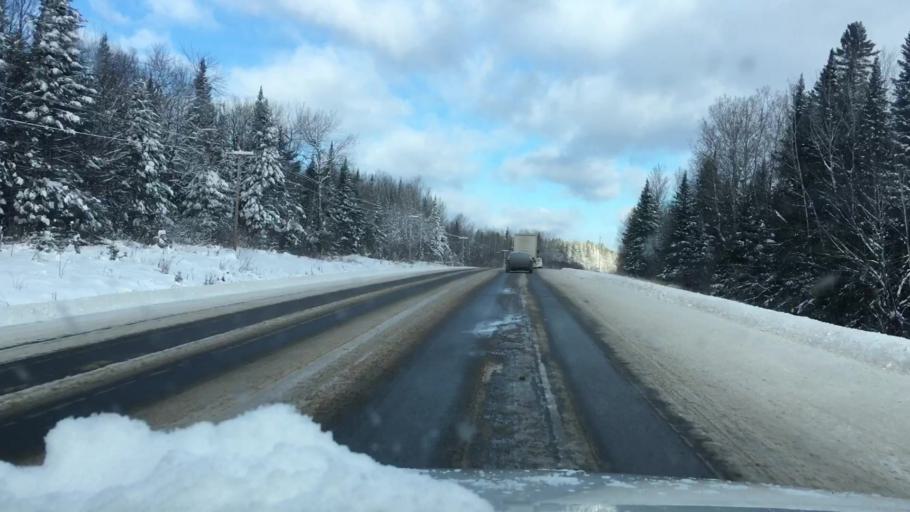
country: US
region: Maine
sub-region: Aroostook County
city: Caribou
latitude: 46.8363
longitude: -67.9991
